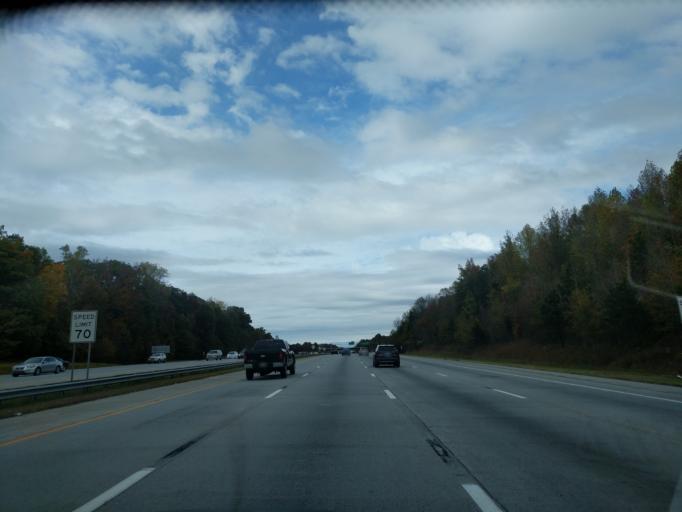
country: US
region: North Carolina
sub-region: Rowan County
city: China Grove
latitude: 35.5929
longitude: -80.5395
